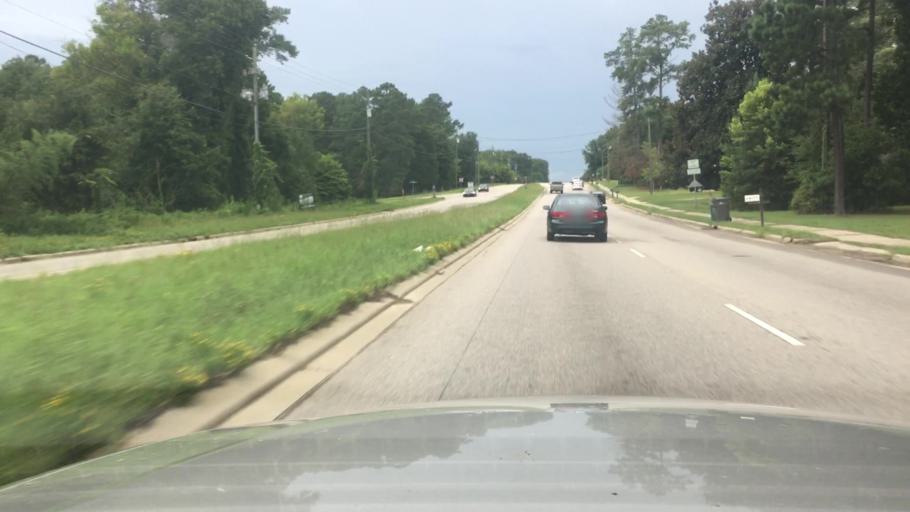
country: US
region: North Carolina
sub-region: Cumberland County
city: Hope Mills
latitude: 34.9969
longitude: -78.9698
